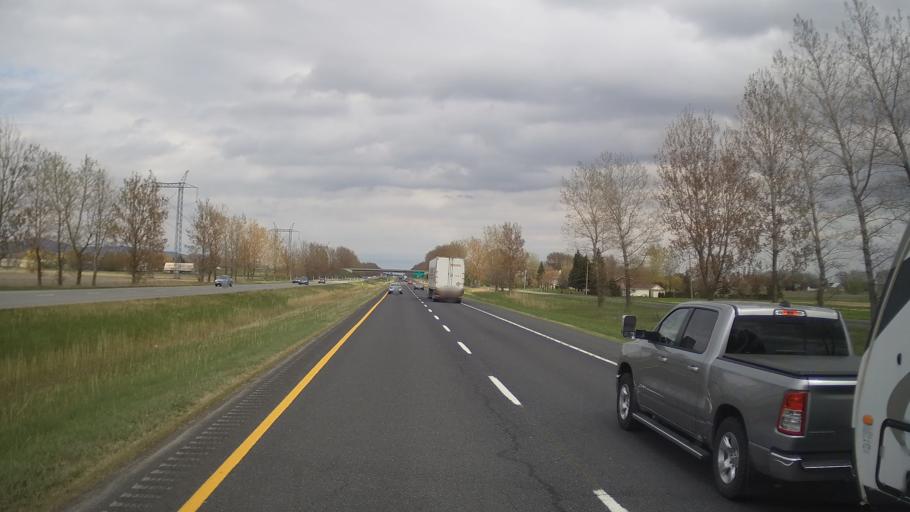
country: CA
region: Quebec
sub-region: Monteregie
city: Marieville
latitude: 45.4014
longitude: -73.1762
